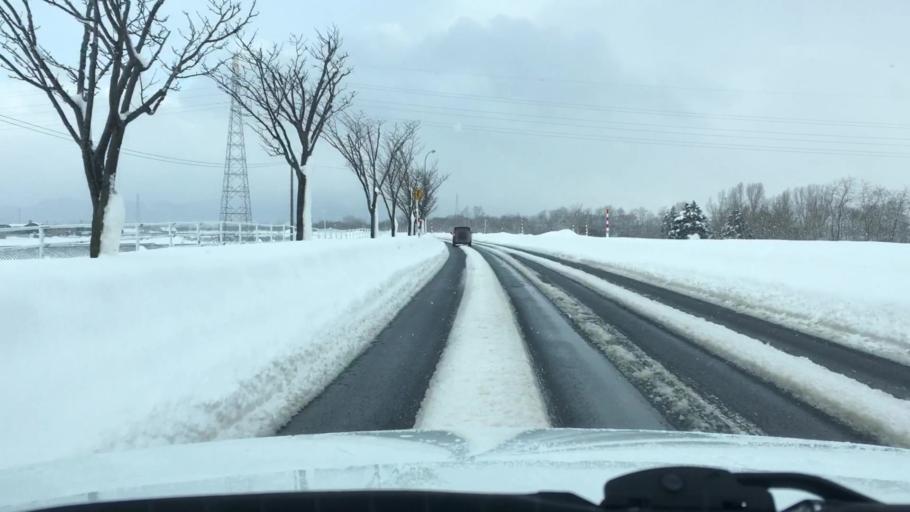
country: JP
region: Aomori
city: Hirosaki
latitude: 40.6401
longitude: 140.4720
